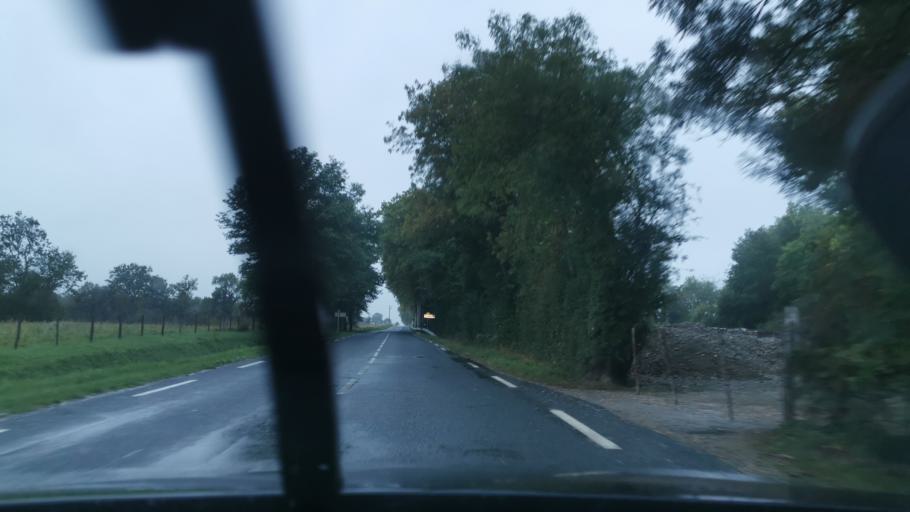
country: FR
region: Rhone-Alpes
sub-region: Departement de l'Ain
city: Amberieux-en-Dombes
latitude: 46.0042
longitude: 4.9030
